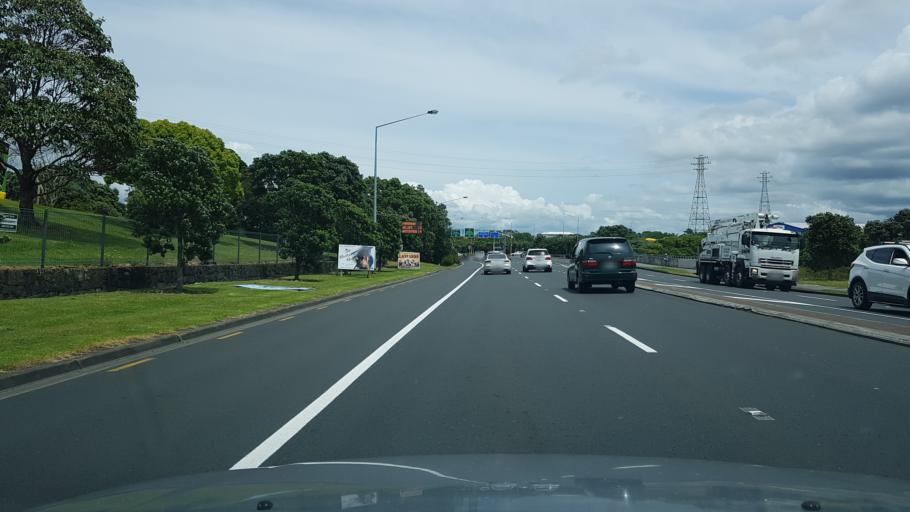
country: NZ
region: Auckland
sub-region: Auckland
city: North Shore
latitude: -36.7959
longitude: 174.7688
